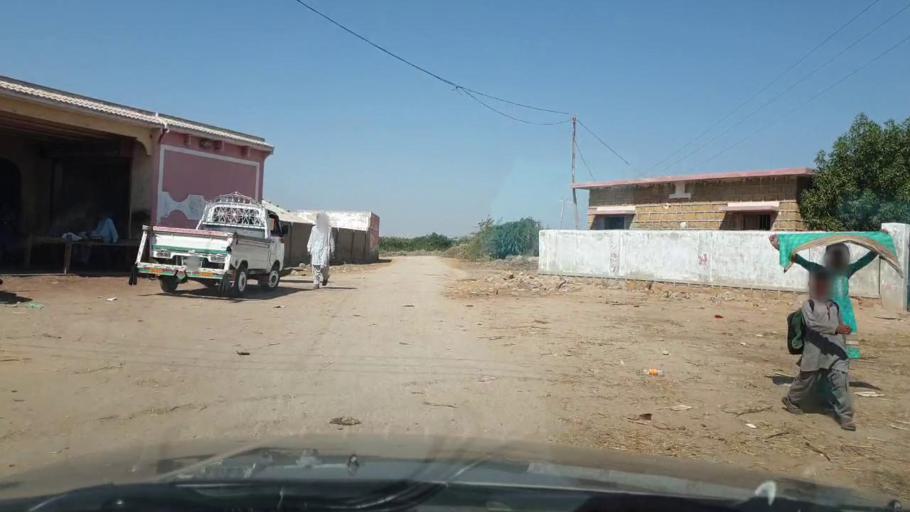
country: PK
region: Sindh
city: Thatta
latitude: 24.6391
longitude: 67.8935
